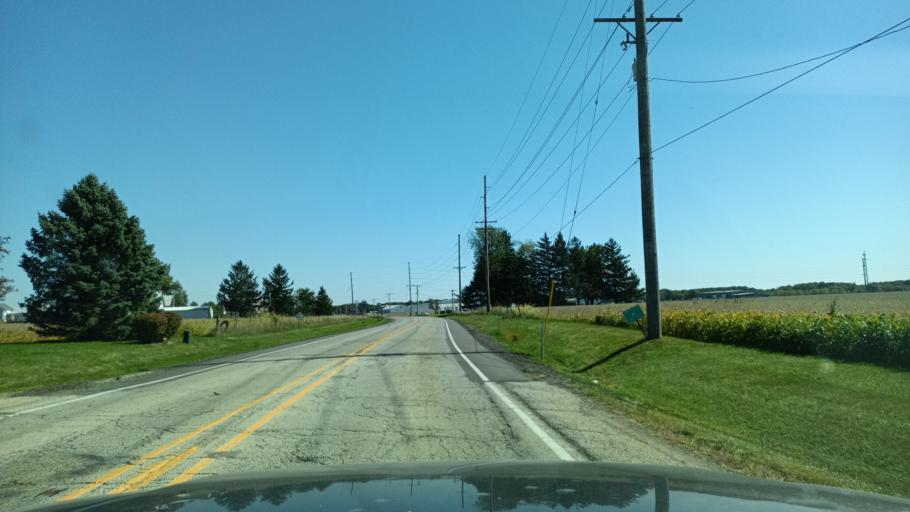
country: US
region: Illinois
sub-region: Woodford County
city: Eureka
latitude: 40.6276
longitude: -89.2731
